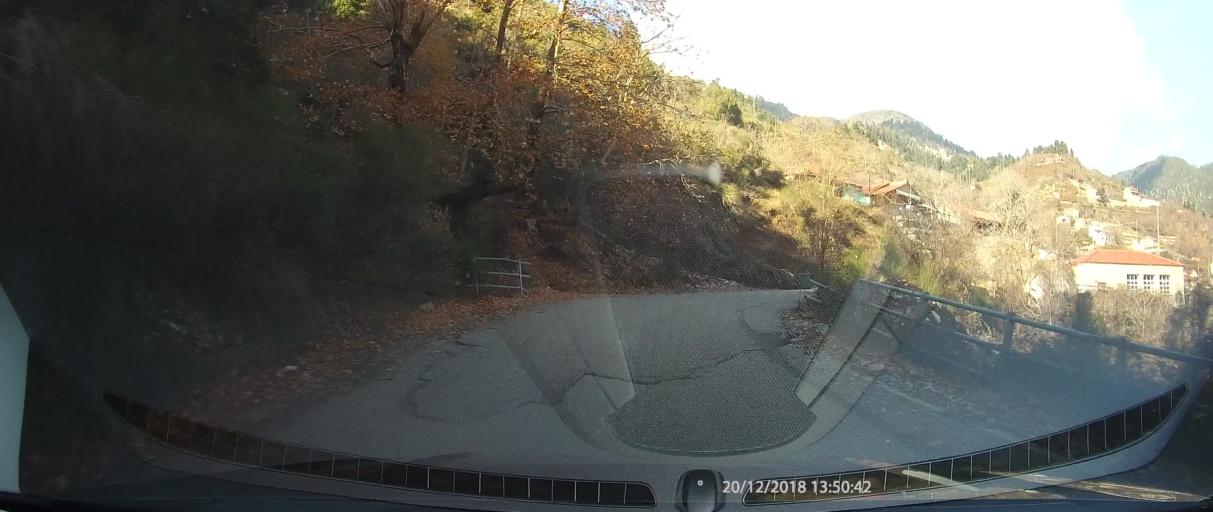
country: GR
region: West Greece
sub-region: Nomos Aitolias kai Akarnanias
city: Paravola
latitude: 38.6993
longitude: 21.6048
